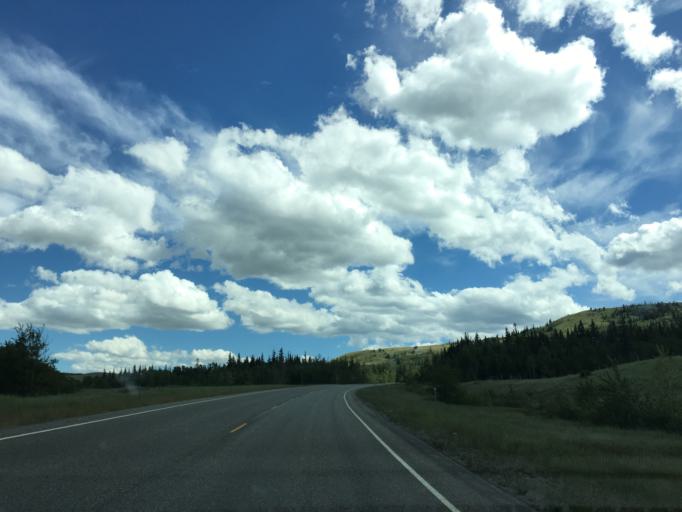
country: US
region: Montana
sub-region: Glacier County
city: Browning
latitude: 48.6069
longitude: -113.2858
